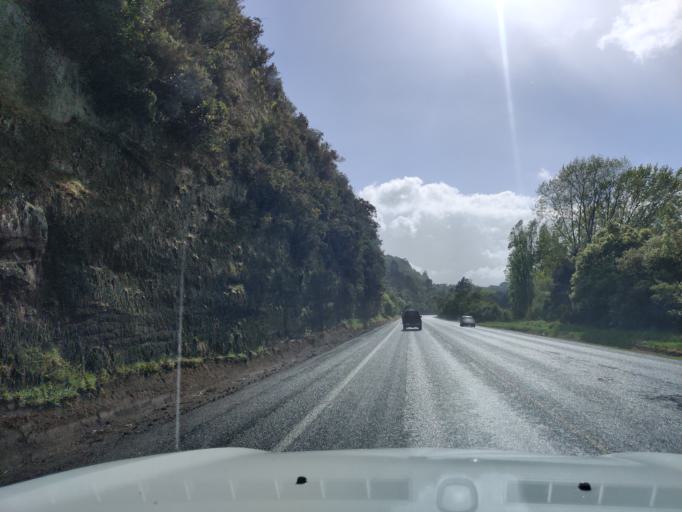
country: NZ
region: Waikato
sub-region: Matamata-Piako District
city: Matamata
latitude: -37.9491
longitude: 175.6379
